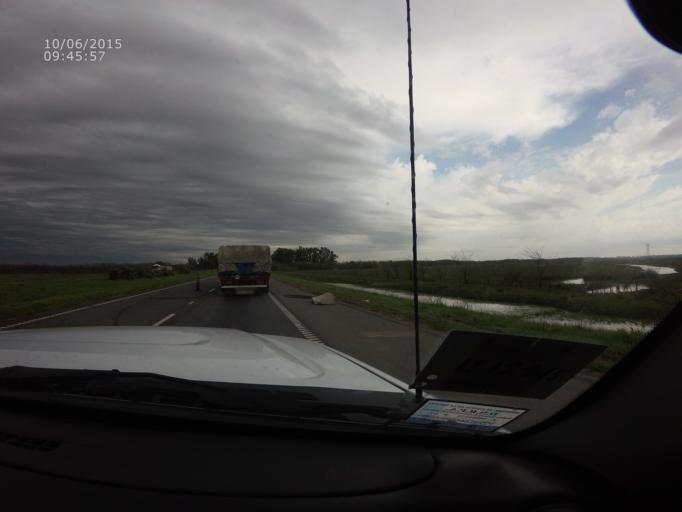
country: AR
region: Buenos Aires
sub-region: San Antonio de Areco
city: San Antonio de Areco
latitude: -34.0572
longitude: -59.2977
